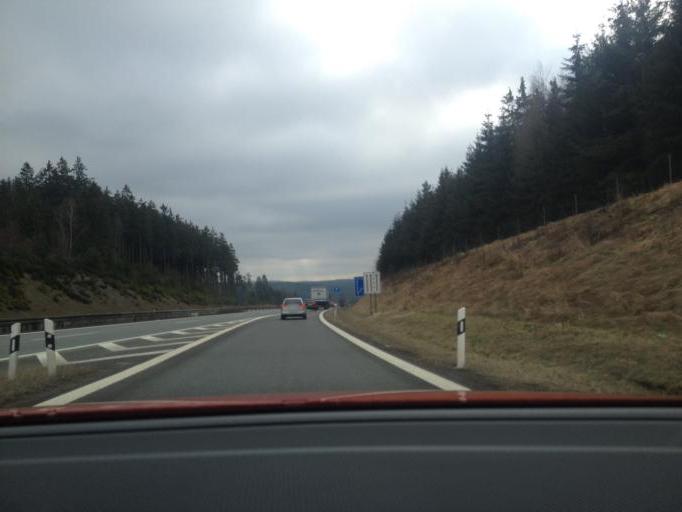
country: DE
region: Bavaria
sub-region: Upper Franconia
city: Rehau
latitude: 50.2668
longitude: 12.0354
